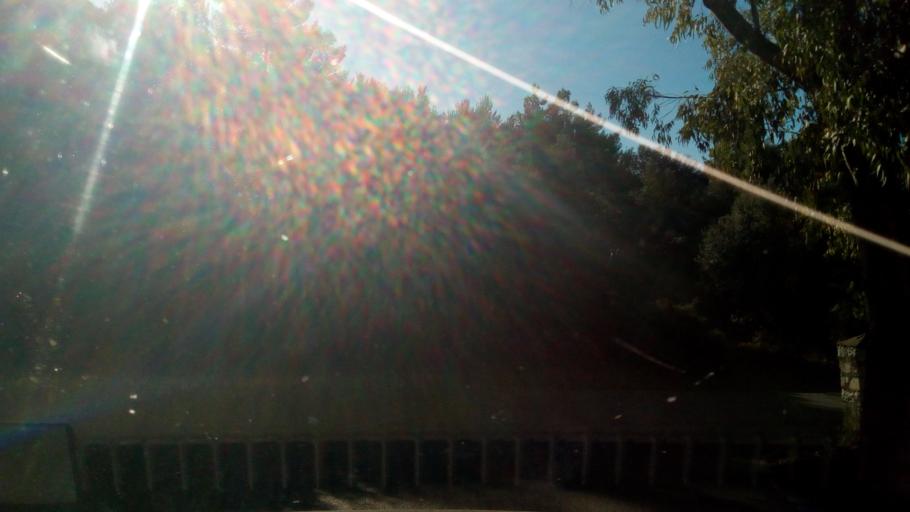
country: GR
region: West Greece
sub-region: Nomos Aitolias kai Akarnanias
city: Nafpaktos
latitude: 38.3942
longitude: 21.8215
